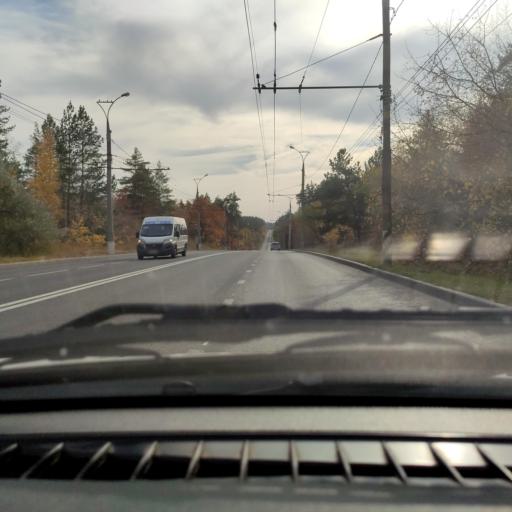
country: RU
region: Samara
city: Zhigulevsk
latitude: 53.5039
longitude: 49.4635
